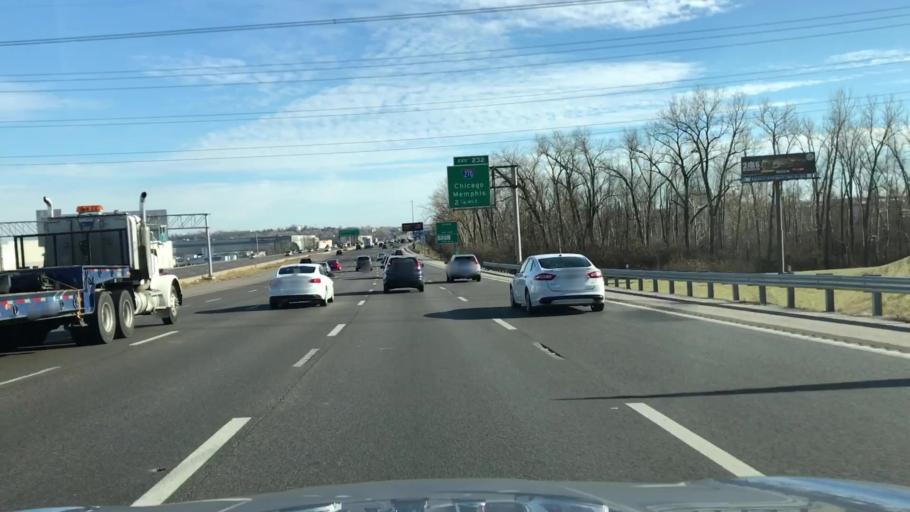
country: US
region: Missouri
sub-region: Saint Charles County
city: Saint Charles
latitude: 38.7620
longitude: -90.4771
